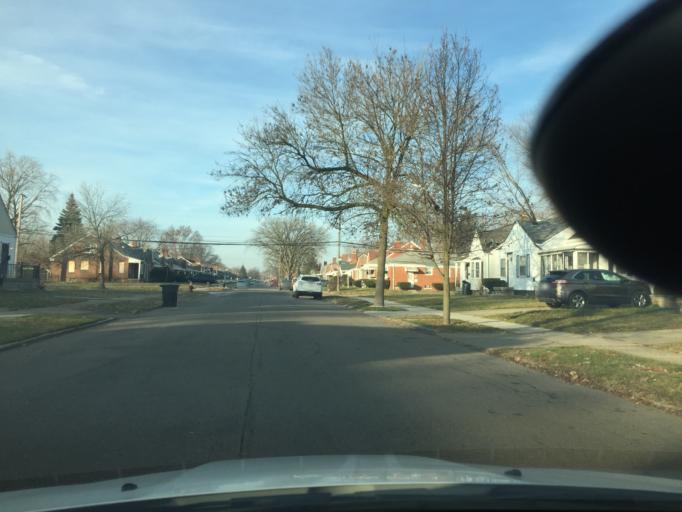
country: US
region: Michigan
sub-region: Macomb County
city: Eastpointe
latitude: 42.4447
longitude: -82.9601
